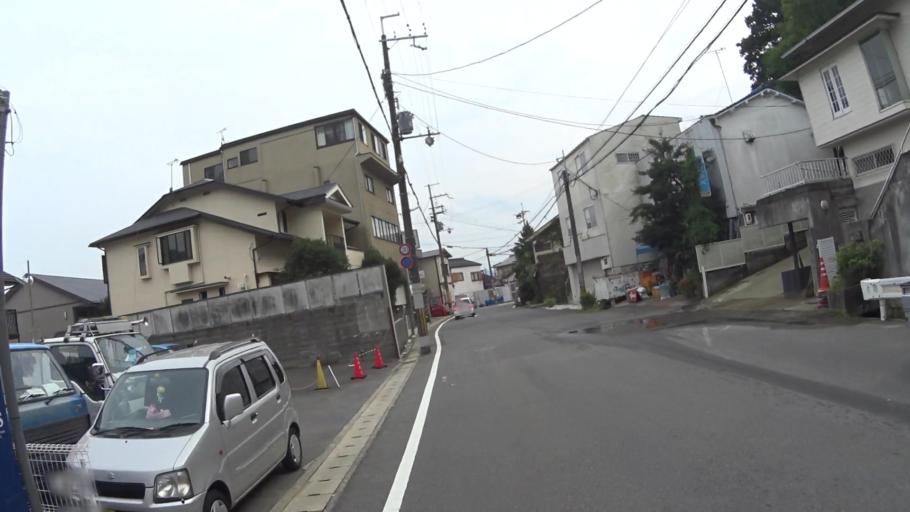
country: JP
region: Kyoto
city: Kyoto
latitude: 34.9955
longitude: 135.7997
